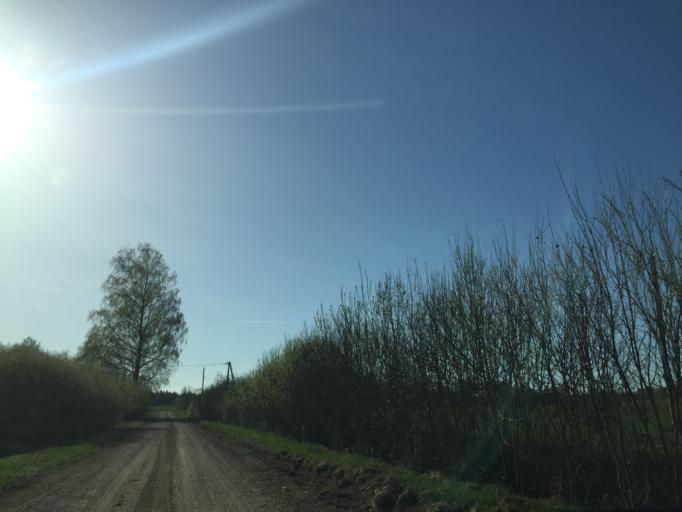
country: LV
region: Ergli
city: Ergli
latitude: 56.8692
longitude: 25.4792
